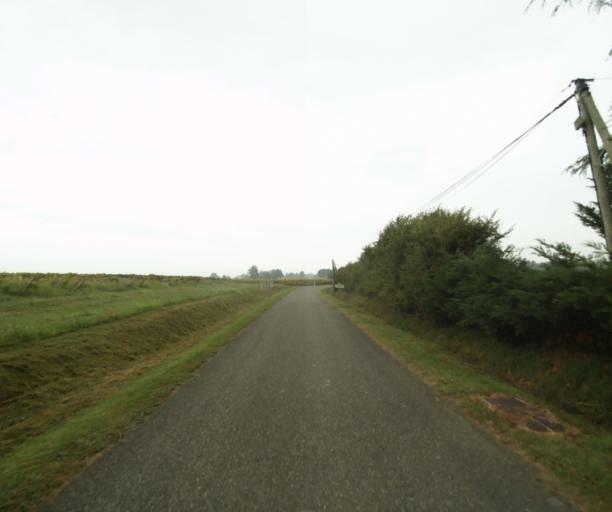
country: FR
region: Midi-Pyrenees
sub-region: Departement du Gers
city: Cazaubon
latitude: 43.9198
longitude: -0.1086
